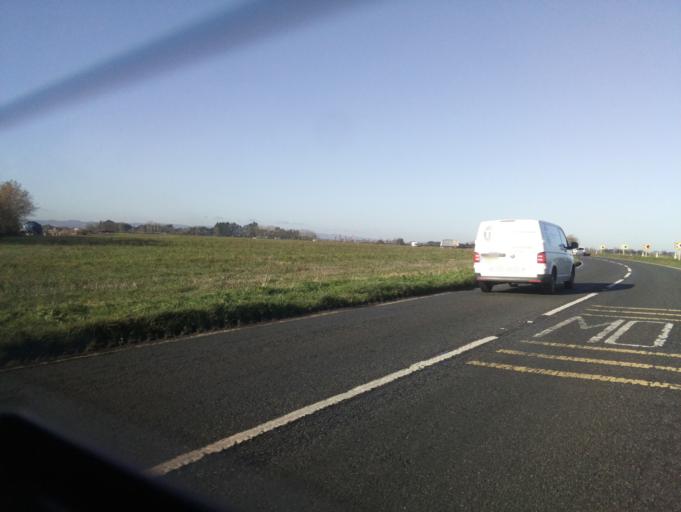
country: GB
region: England
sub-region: Somerset
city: Westonzoyland
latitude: 51.1041
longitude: -2.8982
